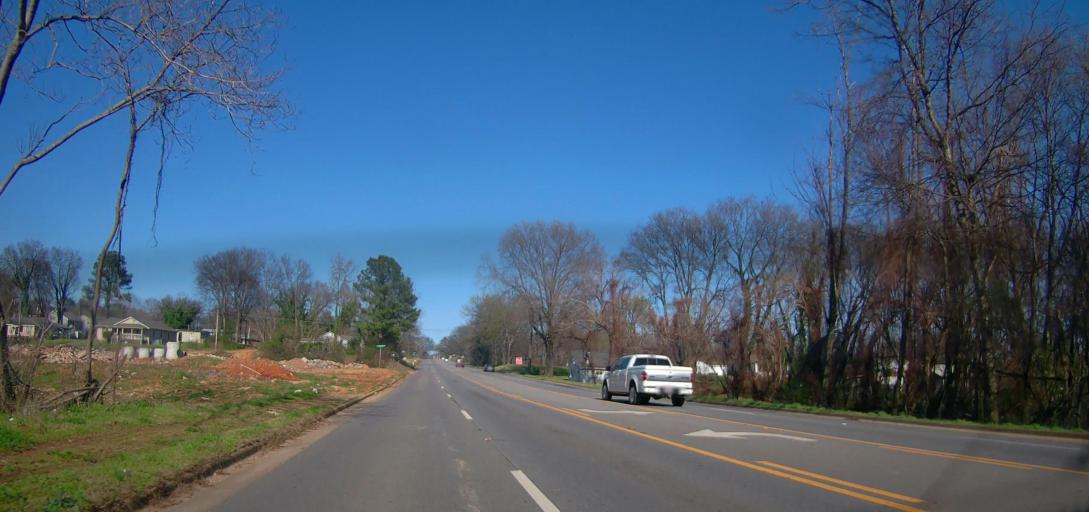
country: US
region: Alabama
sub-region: Lauderdale County
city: East Florence
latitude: 34.8057
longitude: -87.6456
